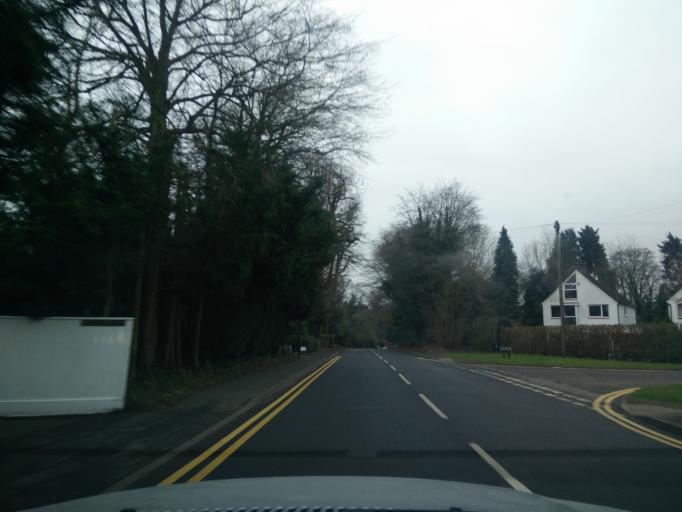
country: GB
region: England
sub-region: Buckinghamshire
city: Little Chalfont
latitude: 51.6644
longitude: -0.5675
